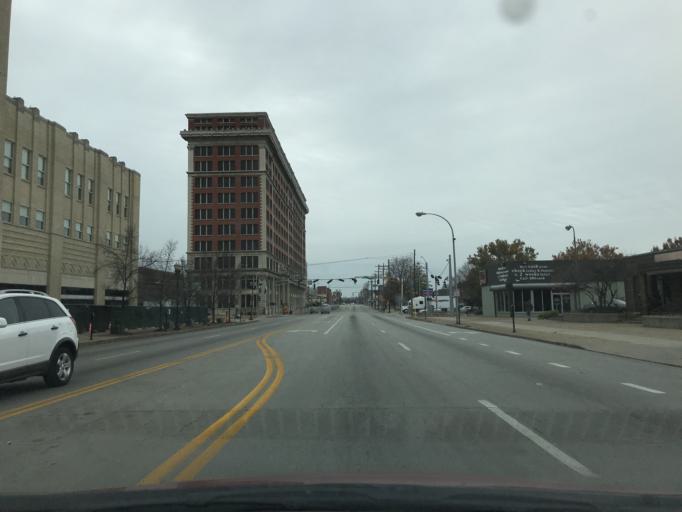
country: US
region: Kentucky
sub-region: Jefferson County
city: Louisville
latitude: 38.2468
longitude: -85.7653
